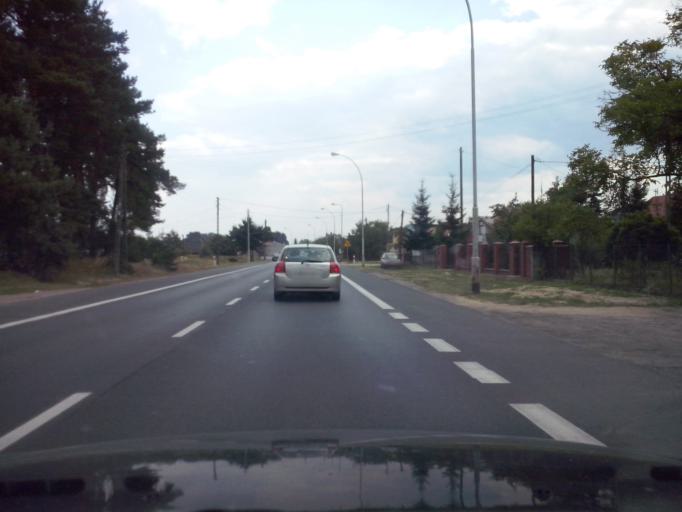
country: PL
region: Subcarpathian Voivodeship
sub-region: Powiat nizanski
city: Nisko
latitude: 50.5312
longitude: 22.1074
